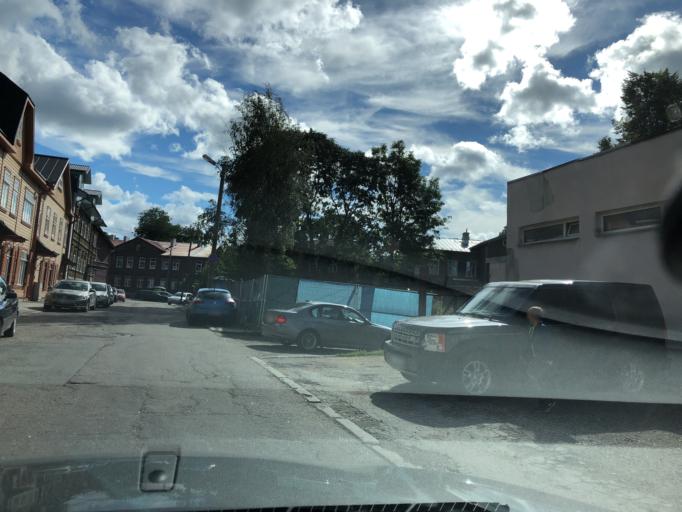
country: EE
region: Harju
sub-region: Tallinna linn
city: Tallinn
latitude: 59.4466
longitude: 24.7336
